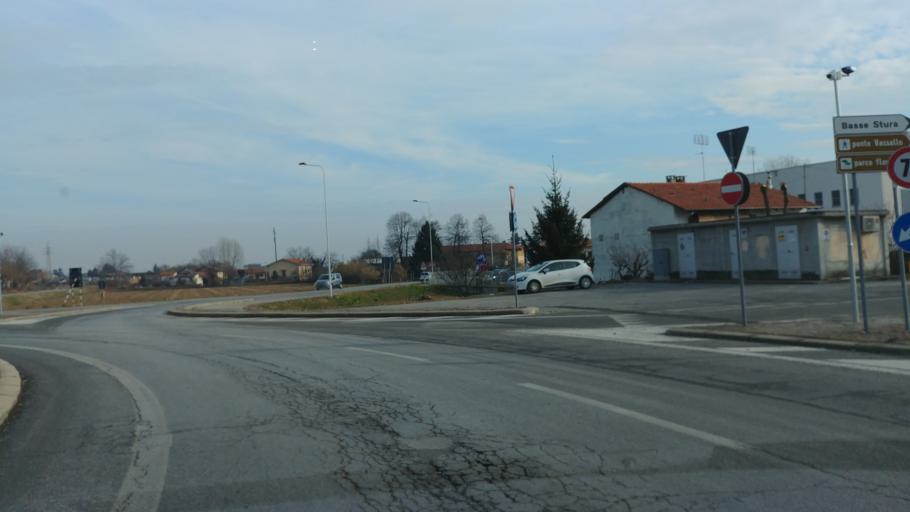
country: IT
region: Piedmont
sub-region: Provincia di Cuneo
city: Cuneo
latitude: 44.3933
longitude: 7.5248
